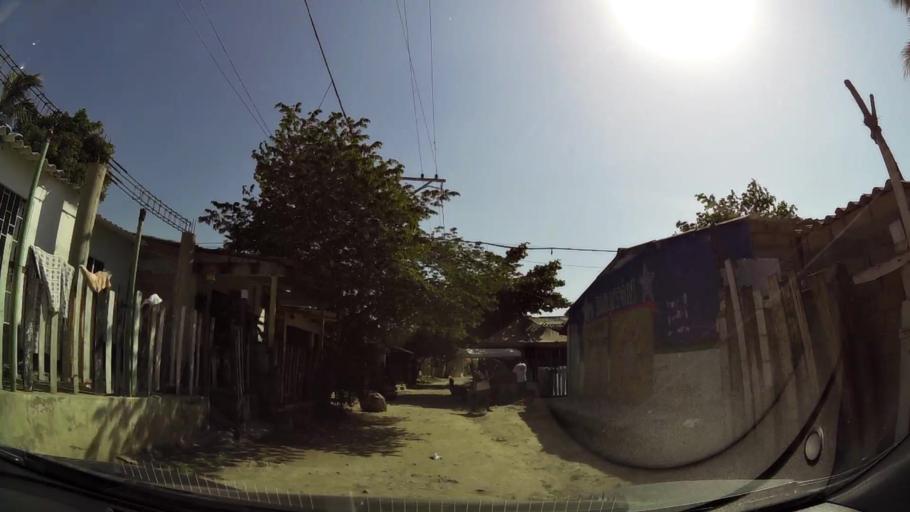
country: CO
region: Bolivar
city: Cartagena
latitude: 10.4146
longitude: -75.5097
